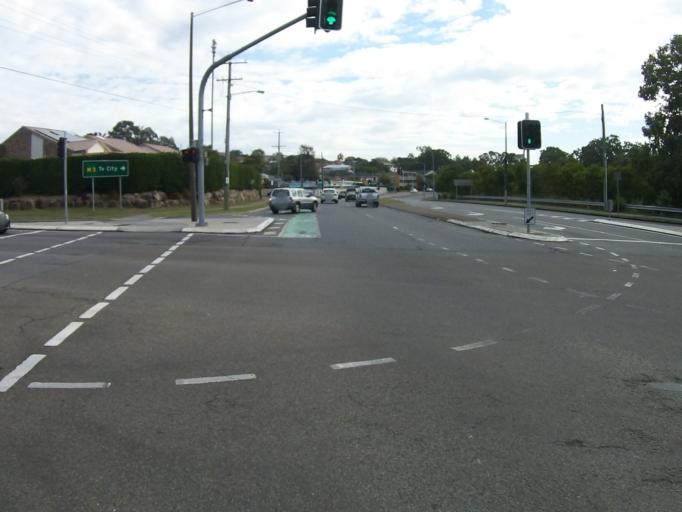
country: AU
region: Queensland
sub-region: Brisbane
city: Greenslopes
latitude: -27.5259
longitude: 153.0553
